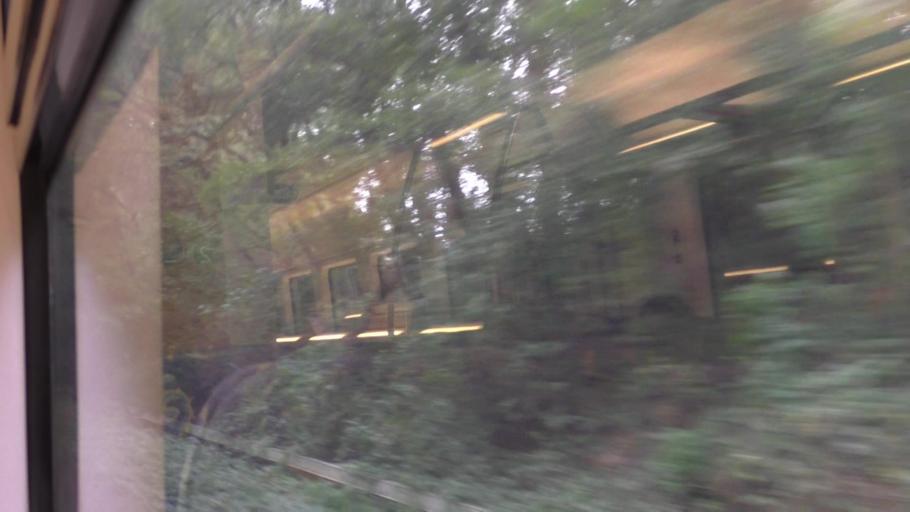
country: DE
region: Saxony
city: Goerlitz
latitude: 51.1781
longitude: 14.9667
